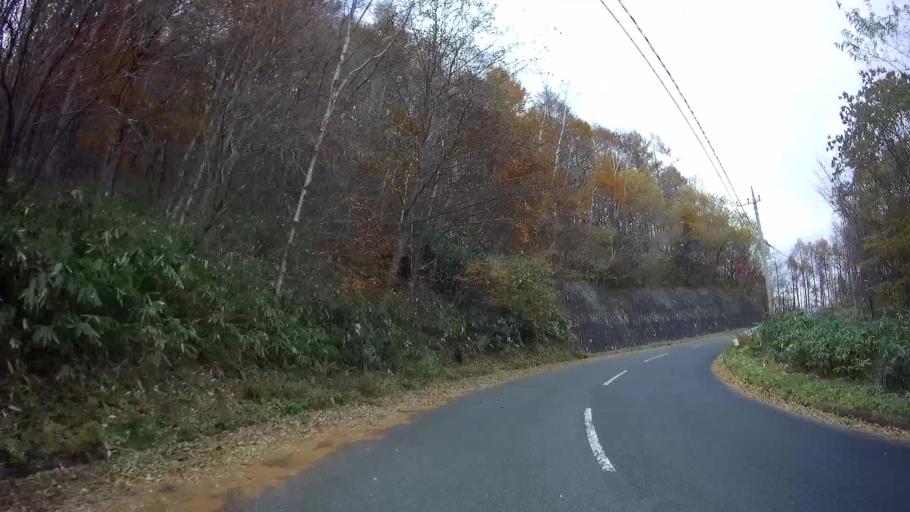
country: JP
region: Gunma
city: Nakanojomachi
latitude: 36.6770
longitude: 138.6631
